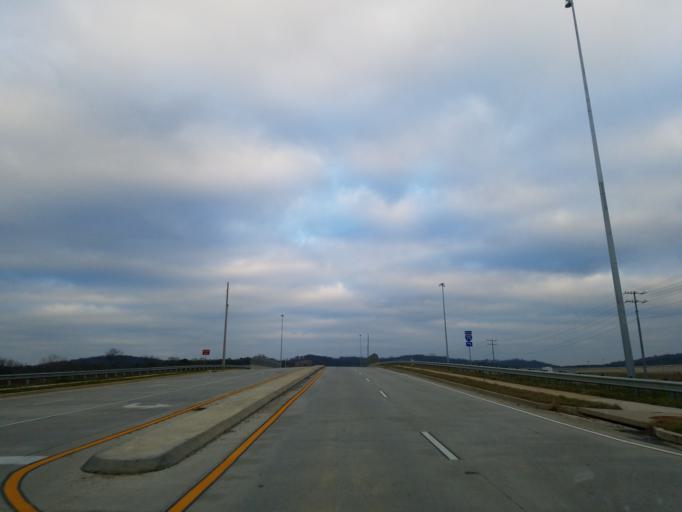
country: US
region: Georgia
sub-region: Gordon County
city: Calhoun
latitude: 34.4419
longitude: -84.9216
